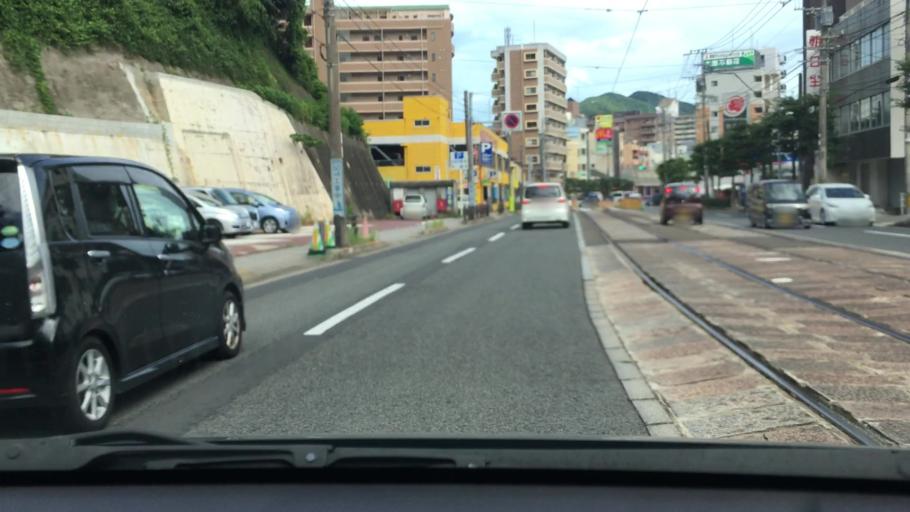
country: JP
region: Nagasaki
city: Obita
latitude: 32.7936
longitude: 129.8581
